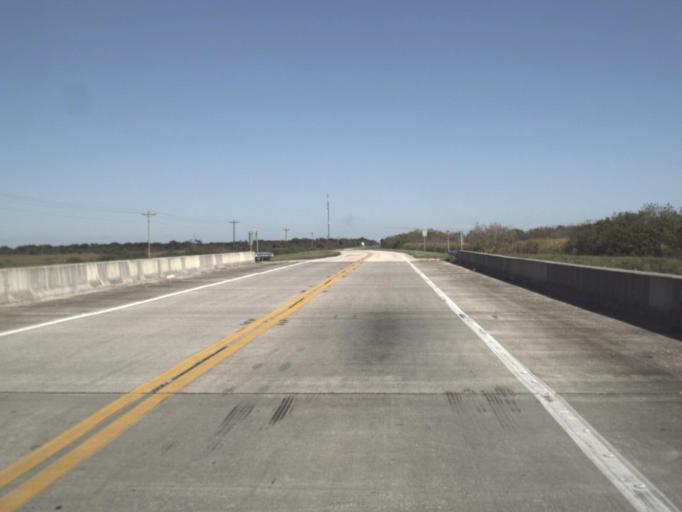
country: US
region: Florida
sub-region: Hendry County
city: Port LaBelle
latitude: 26.7682
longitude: -81.2720
